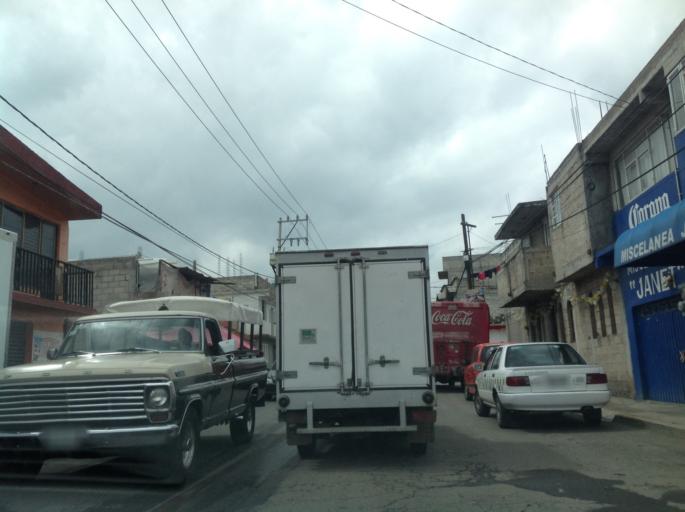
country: MX
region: Mexico
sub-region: Tenango del Valle
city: Santa Maria Jajalpa
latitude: 19.1145
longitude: -99.5376
